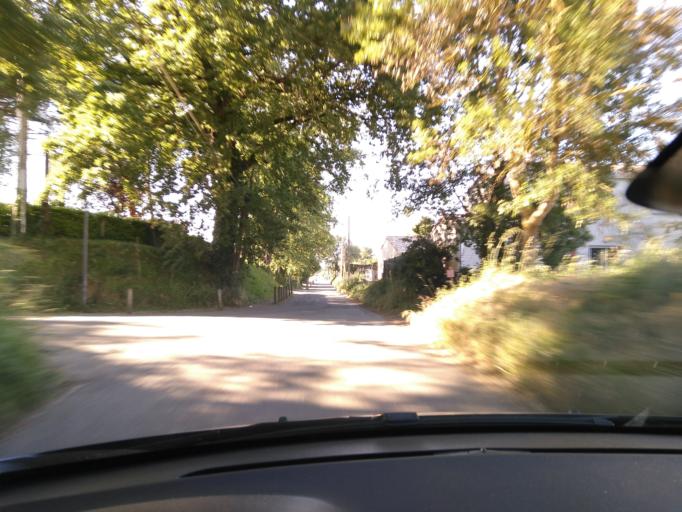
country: FR
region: Midi-Pyrenees
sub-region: Departement de la Haute-Garonne
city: Grenade
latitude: 43.7579
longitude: 1.2984
